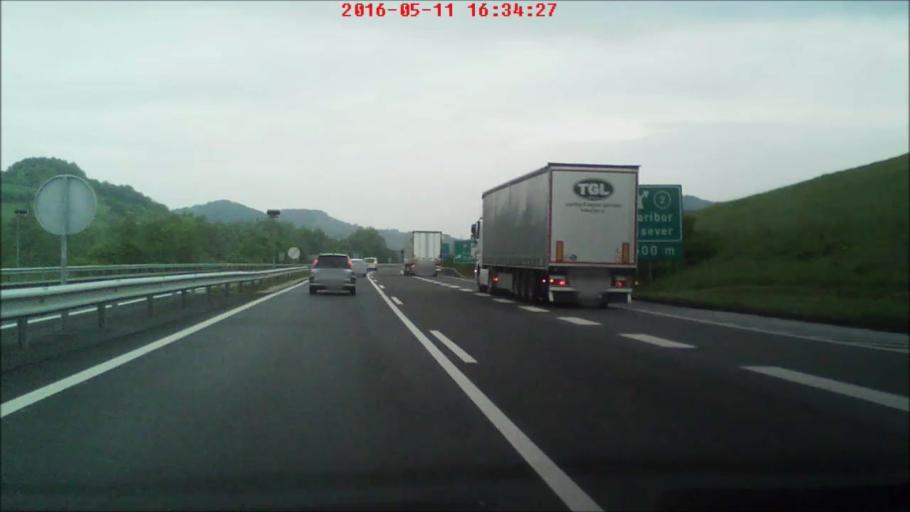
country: SI
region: Pesnica
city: Pesnica pri Mariboru
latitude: 46.6144
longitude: 15.6616
